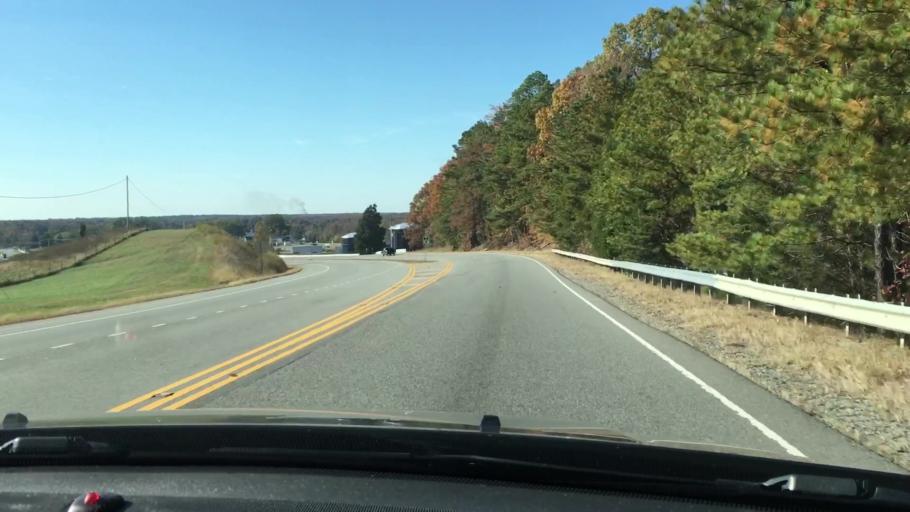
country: US
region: Virginia
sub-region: Hanover County
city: Hanover
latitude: 37.8510
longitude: -77.4095
